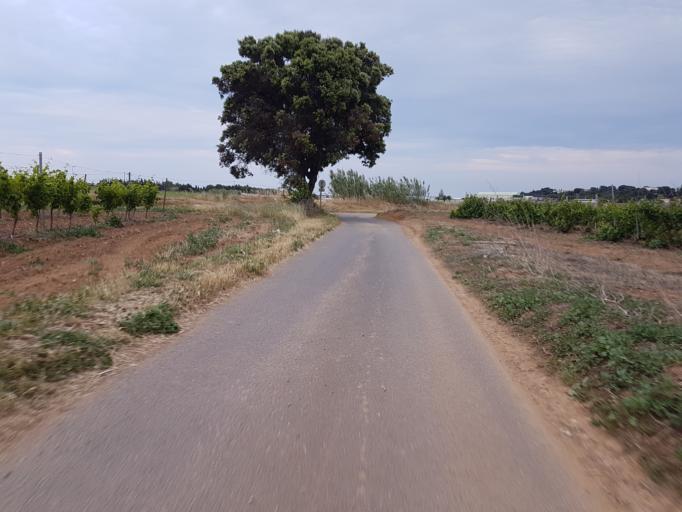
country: FR
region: Languedoc-Roussillon
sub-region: Departement de l'Herault
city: Portiragnes
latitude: 43.3160
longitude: 3.3351
